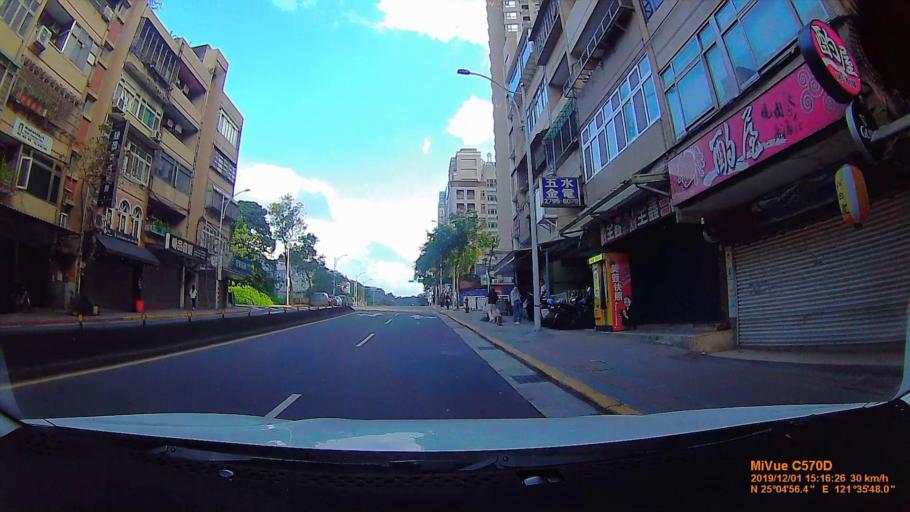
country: TW
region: Taipei
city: Taipei
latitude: 25.0822
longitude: 121.5968
